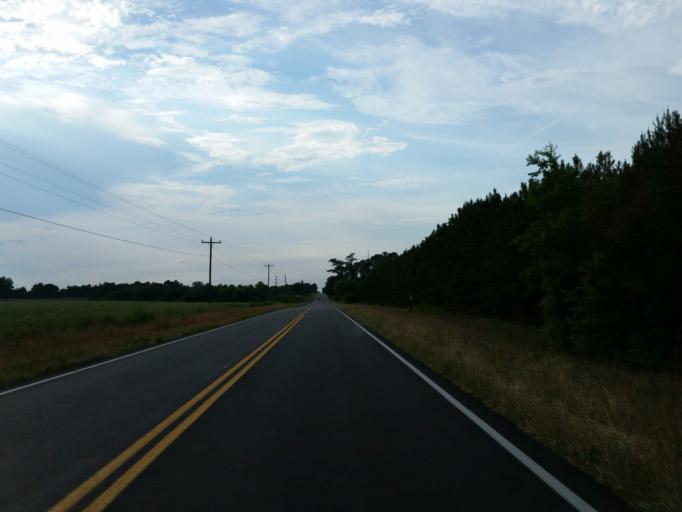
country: US
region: Georgia
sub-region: Dooly County
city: Unadilla
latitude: 32.2880
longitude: -83.7501
